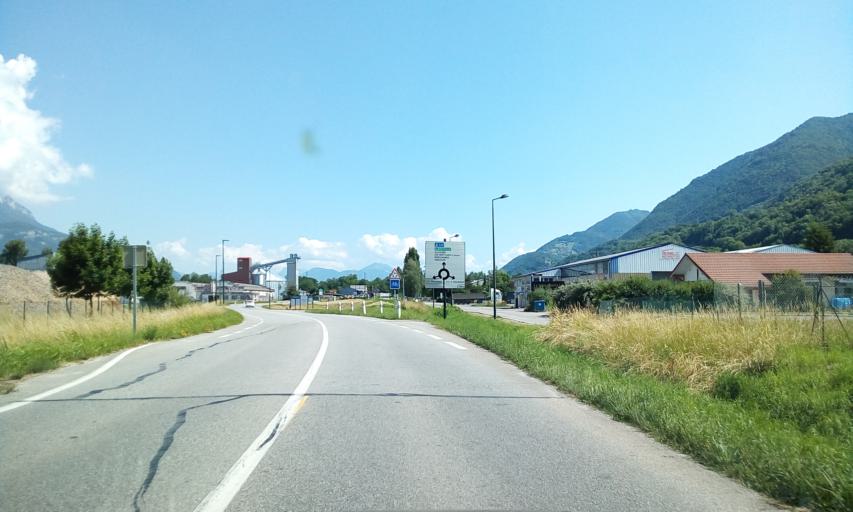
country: FR
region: Rhone-Alpes
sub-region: Departement de l'Isere
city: Tencin
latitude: 45.3265
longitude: 5.9689
